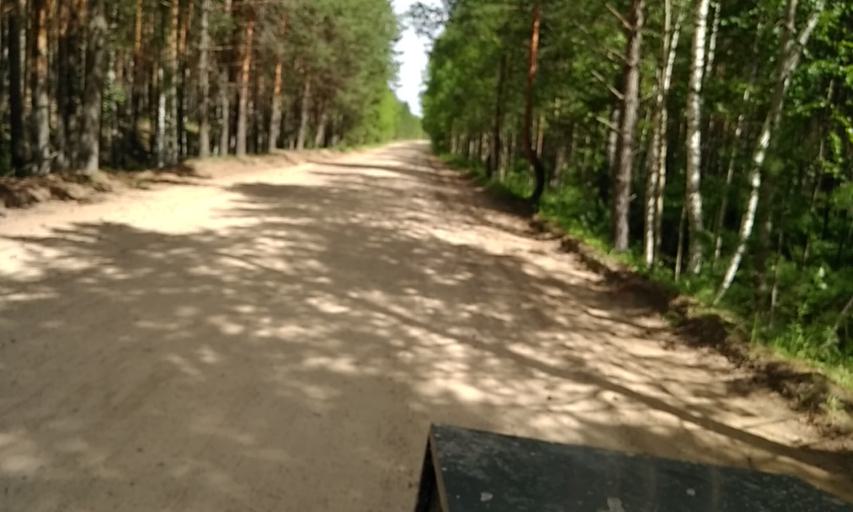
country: RU
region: Tomsk
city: Timiryazevskoye
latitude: 56.4203
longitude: 84.6794
